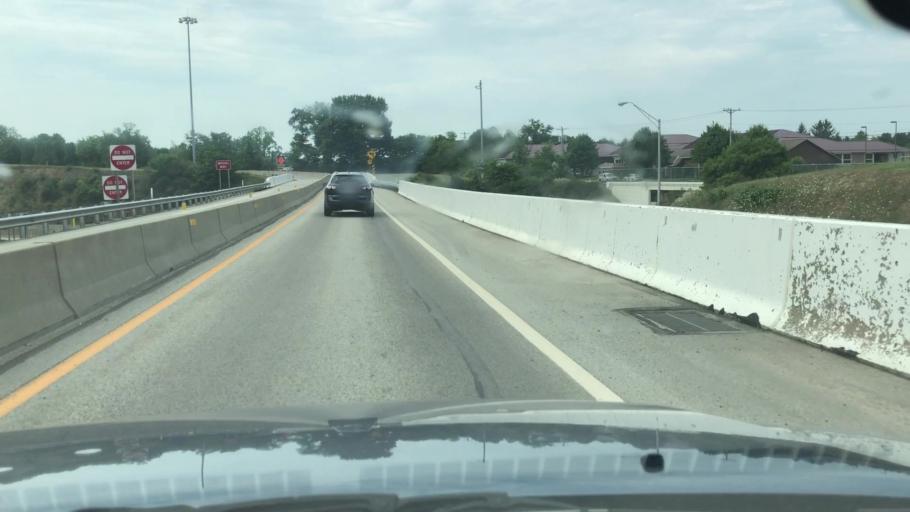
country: US
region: Pennsylvania
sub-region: Allegheny County
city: Gibsonia
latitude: 40.6099
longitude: -79.9466
